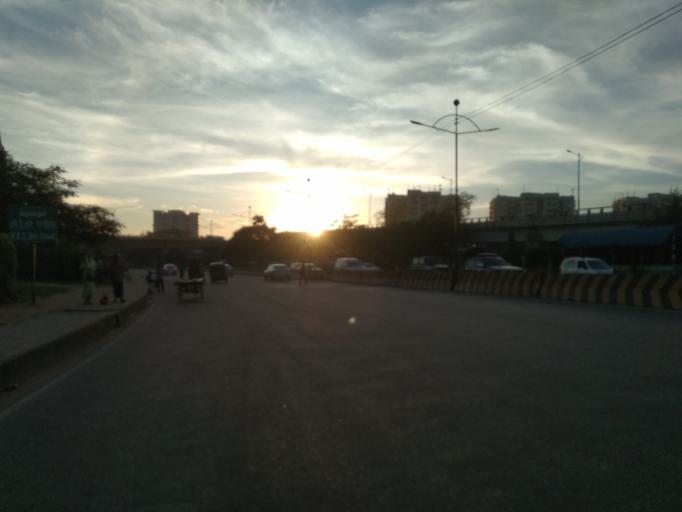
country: BD
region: Dhaka
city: Tungi
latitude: 23.8169
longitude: 90.4065
